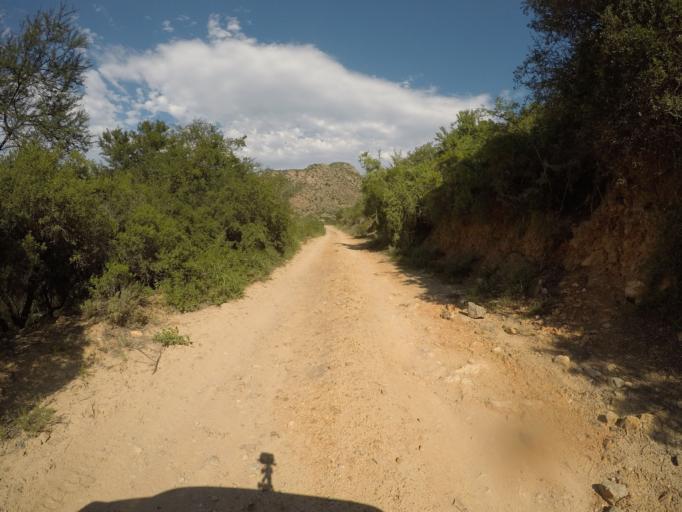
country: ZA
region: Eastern Cape
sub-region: Cacadu District Municipality
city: Kareedouw
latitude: -33.6537
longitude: 24.4184
